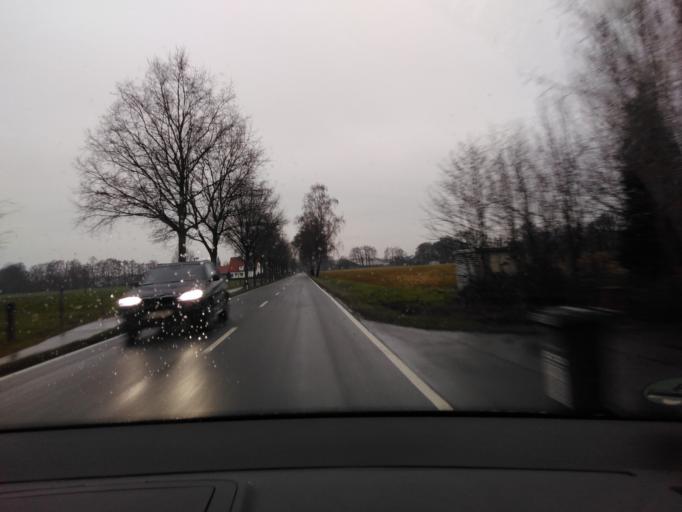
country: DE
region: North Rhine-Westphalia
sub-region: Regierungsbezirk Detmold
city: Verl
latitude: 51.8907
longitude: 8.4826
